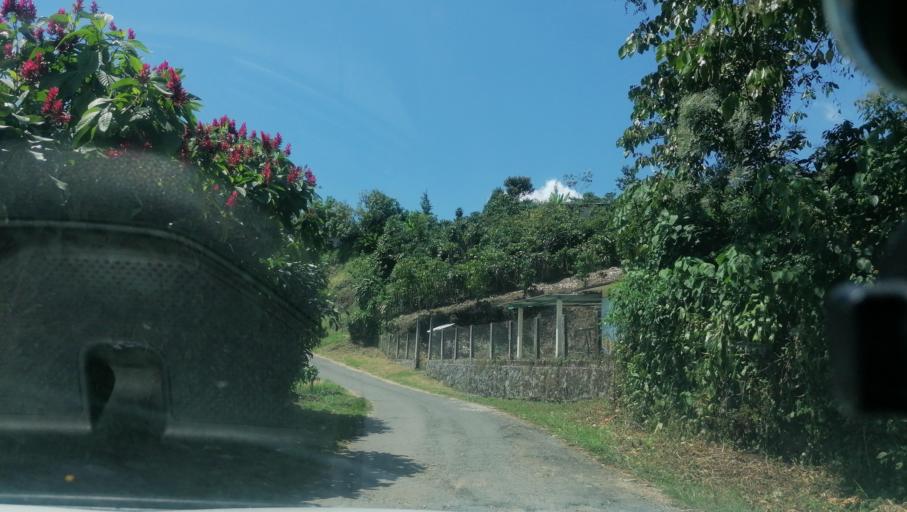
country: MX
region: Chiapas
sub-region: Cacahoatan
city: Benito Juarez
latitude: 15.0635
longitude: -92.1427
